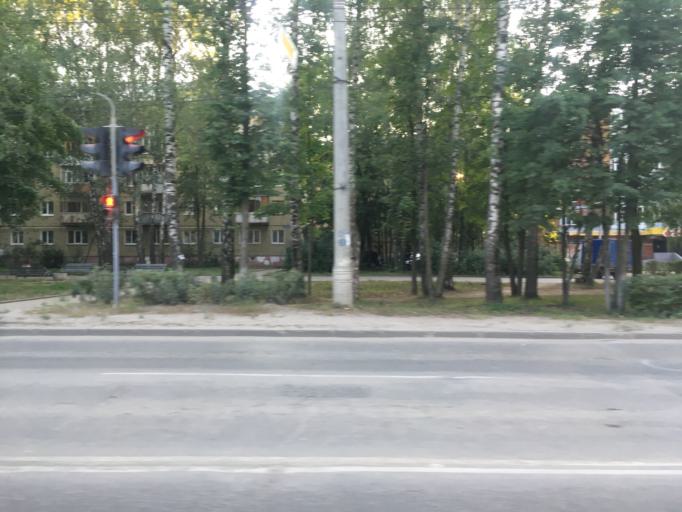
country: RU
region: Mariy-El
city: Yoshkar-Ola
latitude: 56.6491
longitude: 47.8748
